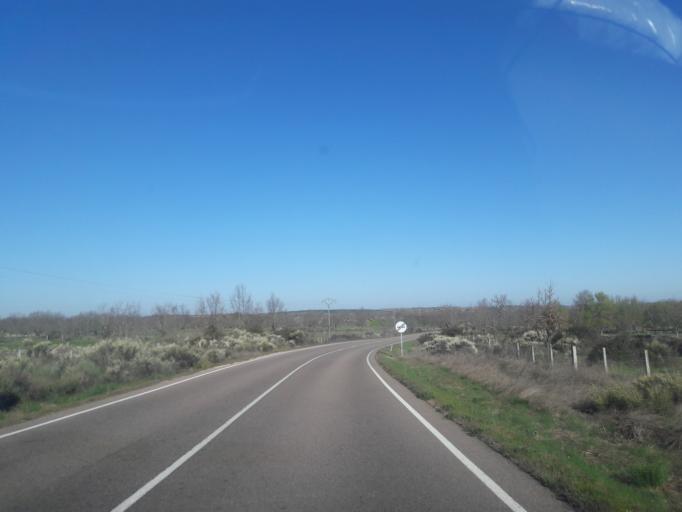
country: ES
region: Castille and Leon
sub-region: Provincia de Salamanca
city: Guadramiro
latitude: 41.0284
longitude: -6.4625
